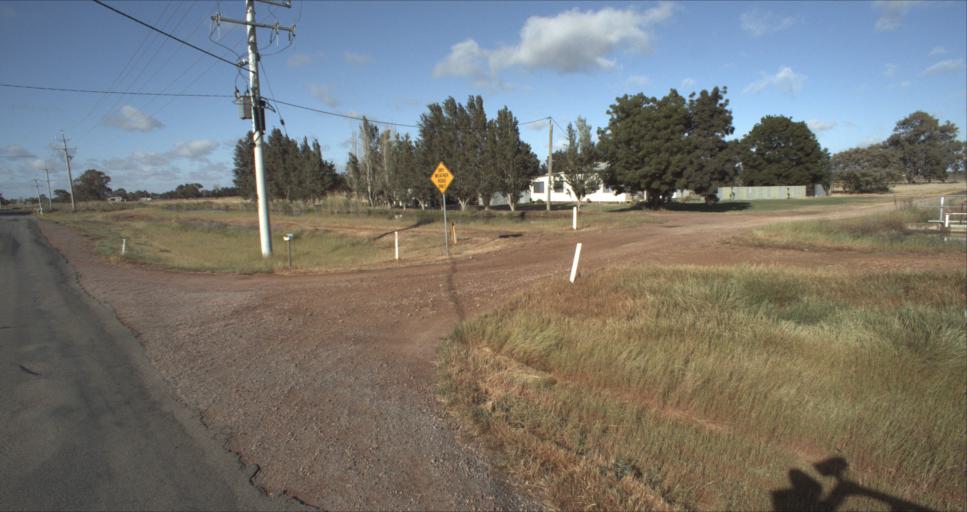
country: AU
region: New South Wales
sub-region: Leeton
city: Leeton
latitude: -34.5310
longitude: 146.3887
